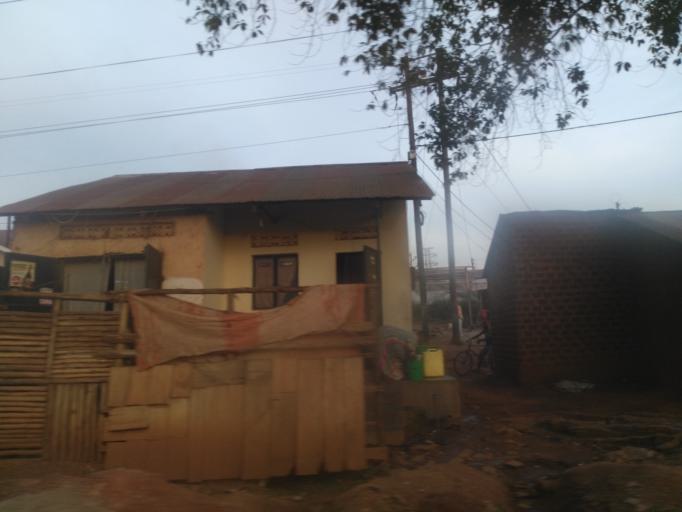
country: UG
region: Central Region
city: Kampala Central Division
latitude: 0.3467
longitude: 32.5733
